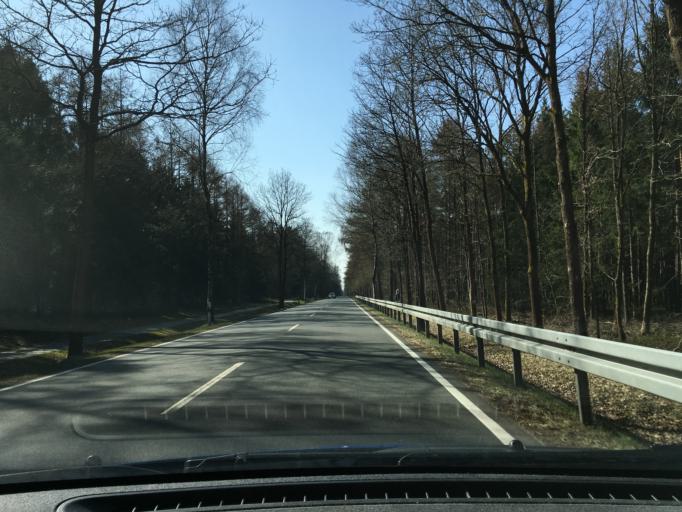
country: DE
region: Lower Saxony
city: Hermannsburg
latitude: 52.8219
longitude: 10.1630
